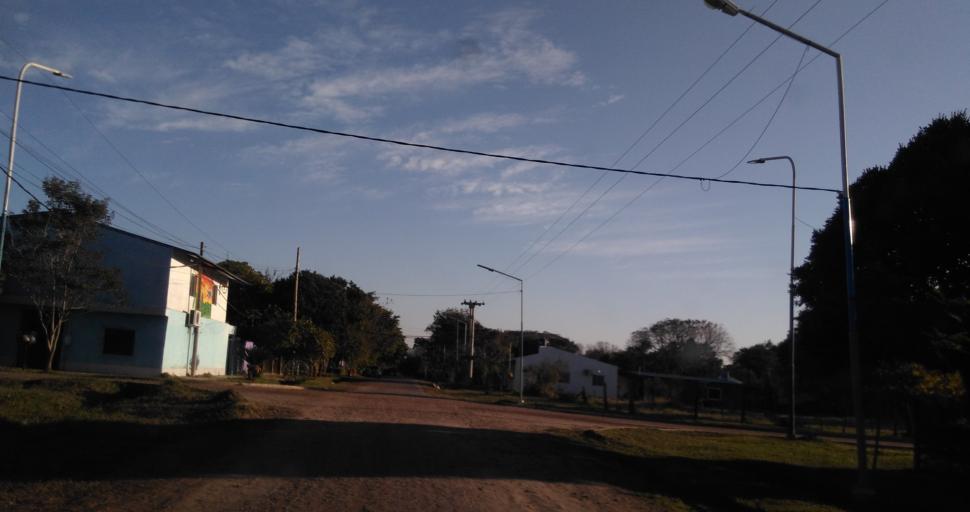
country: AR
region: Chaco
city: Colonia Benitez
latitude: -27.3301
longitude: -58.9456
